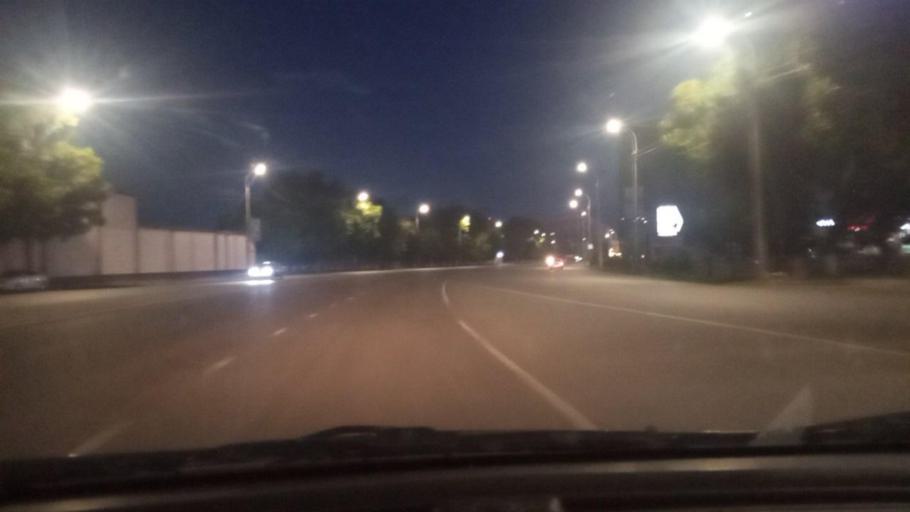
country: UZ
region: Toshkent Shahri
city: Tashkent
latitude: 41.2690
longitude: 69.2607
